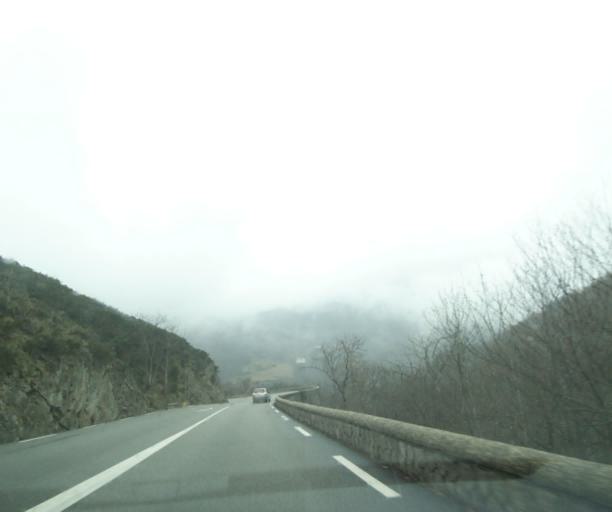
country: FR
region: Rhone-Alpes
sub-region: Departement de l'Ardeche
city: Thueyts
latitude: 44.6727
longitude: 4.0962
